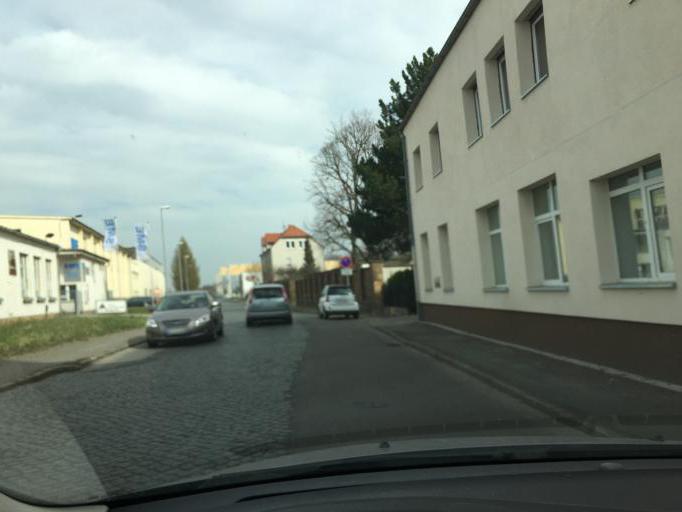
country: DE
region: Saxony
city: Taucha
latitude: 51.3490
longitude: 12.4939
